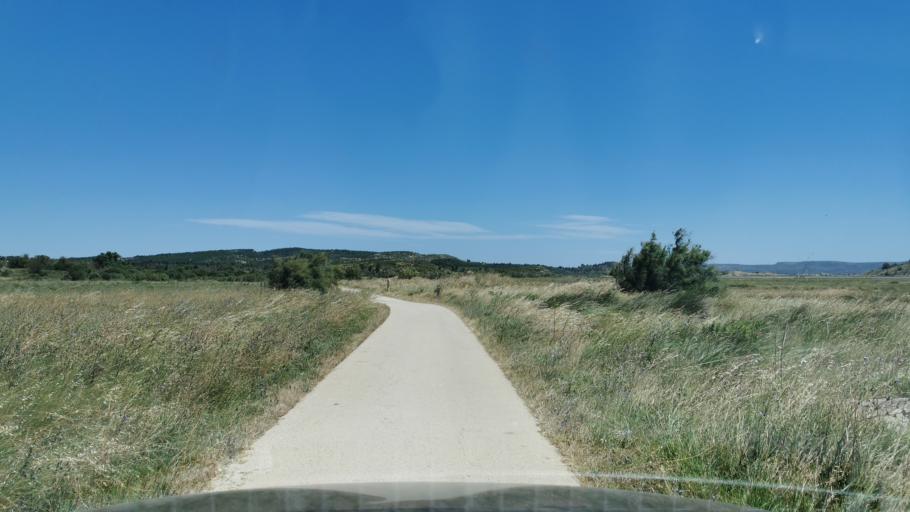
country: FR
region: Languedoc-Roussillon
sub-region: Departement de l'Aude
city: Peyriac-de-Mer
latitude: 43.0983
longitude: 2.9581
